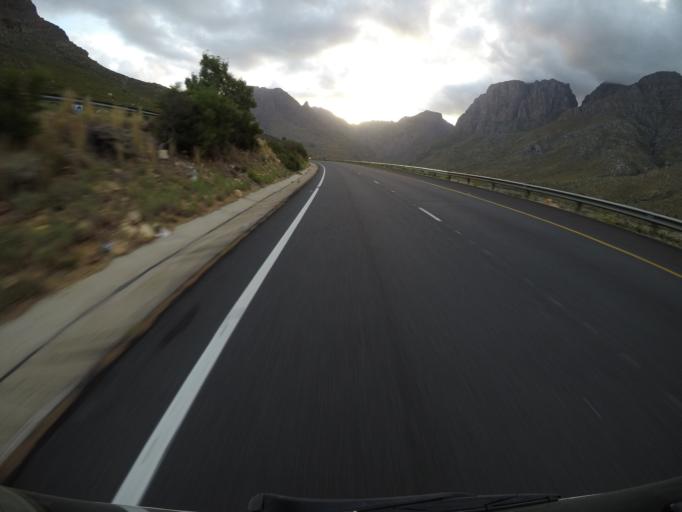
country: ZA
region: Western Cape
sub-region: Cape Winelands District Municipality
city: Worcester
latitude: -33.6997
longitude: 19.2177
